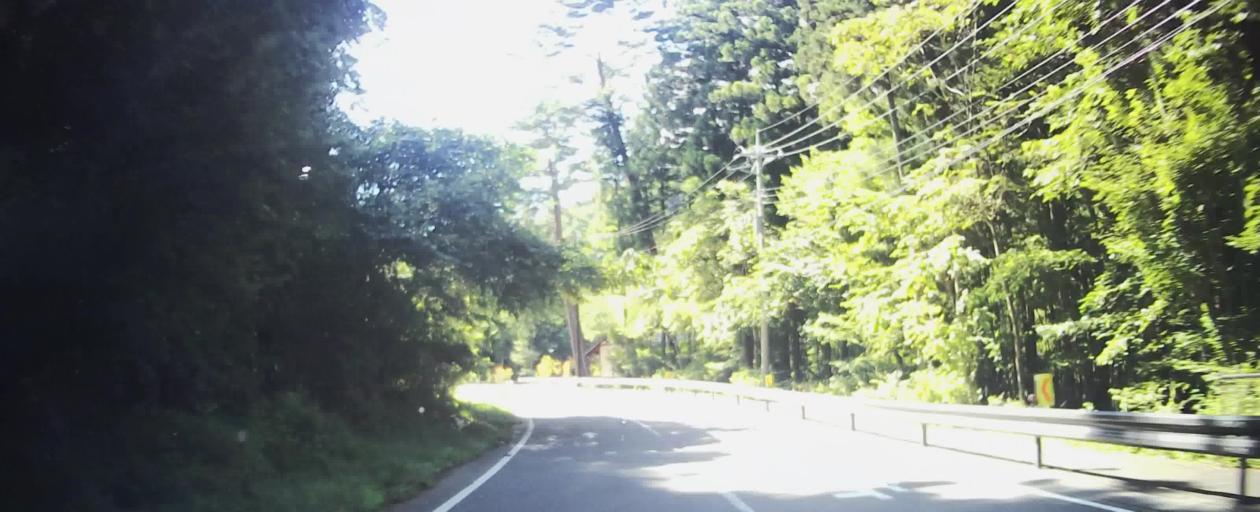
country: JP
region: Gunma
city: Nakanojomachi
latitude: 36.5633
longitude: 138.7259
